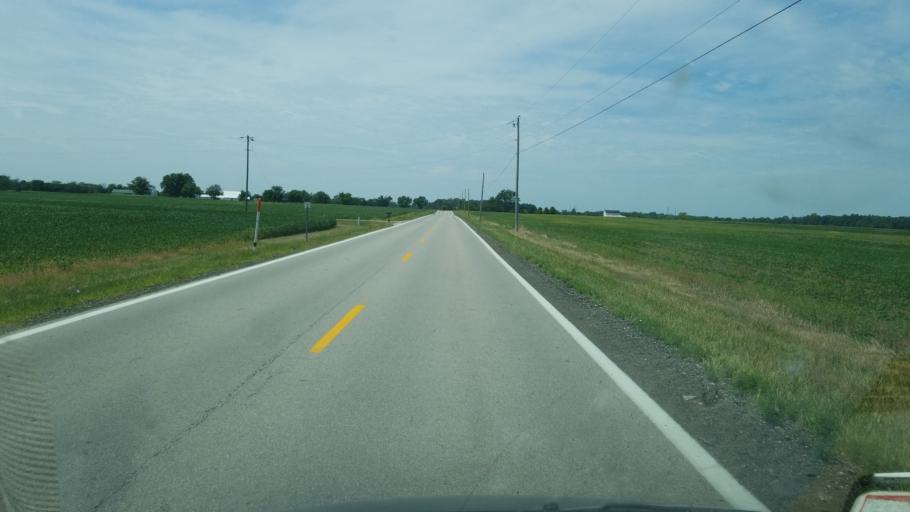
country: US
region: Ohio
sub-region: Madison County
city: West Jefferson
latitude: 39.8781
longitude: -83.3213
